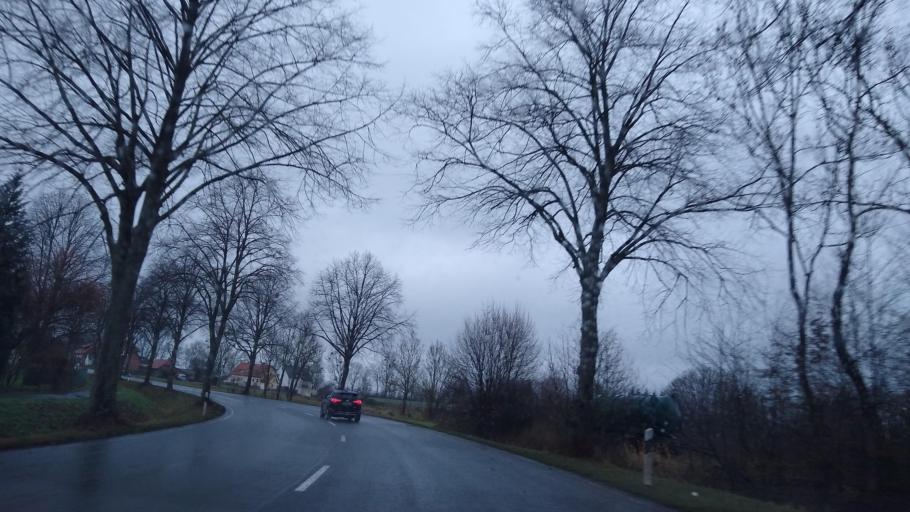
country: DE
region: Lower Saxony
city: Holzen
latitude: 51.9184
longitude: 9.6661
